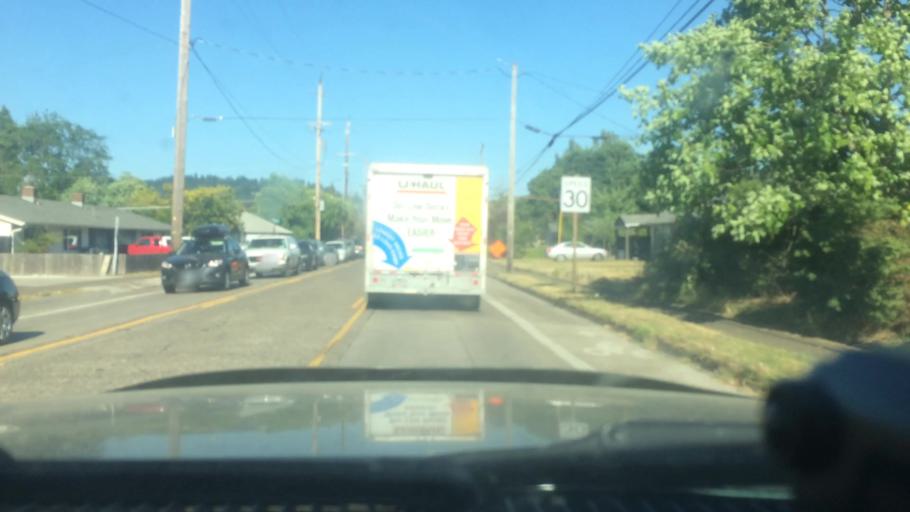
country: US
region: Oregon
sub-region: Lane County
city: Eugene
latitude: 44.0262
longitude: -123.0897
